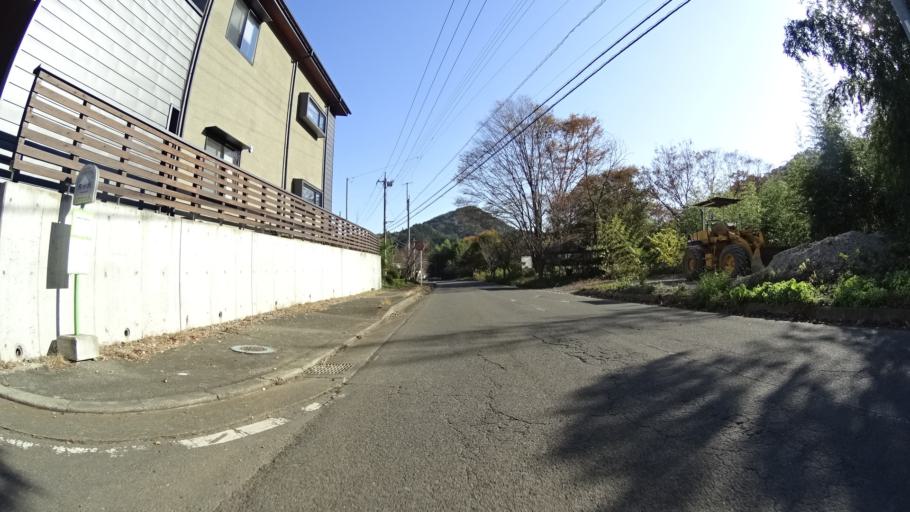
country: JP
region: Yamanashi
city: Uenohara
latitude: 35.6454
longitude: 139.1254
